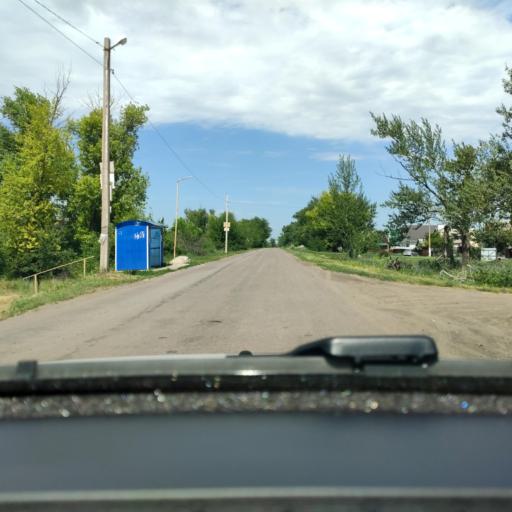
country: RU
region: Voronezj
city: Maslovka
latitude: 51.5112
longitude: 39.2955
